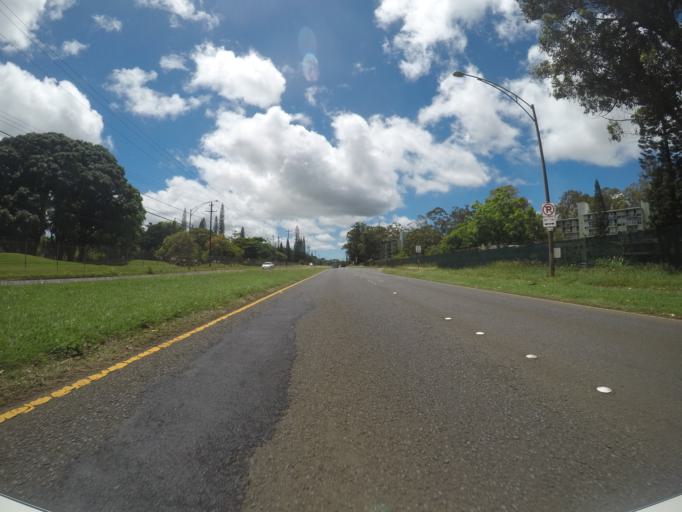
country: US
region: Hawaii
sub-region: Honolulu County
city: Schofield Barracks
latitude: 21.4920
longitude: -158.0469
